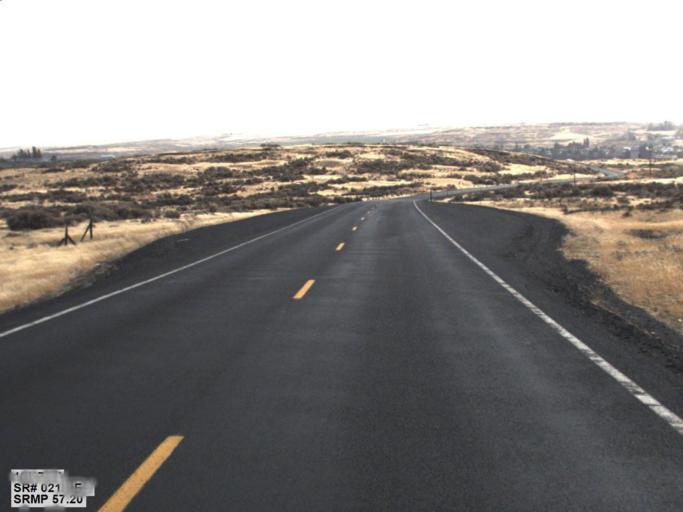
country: US
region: Washington
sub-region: Adams County
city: Ritzville
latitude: 47.3498
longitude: -118.6949
